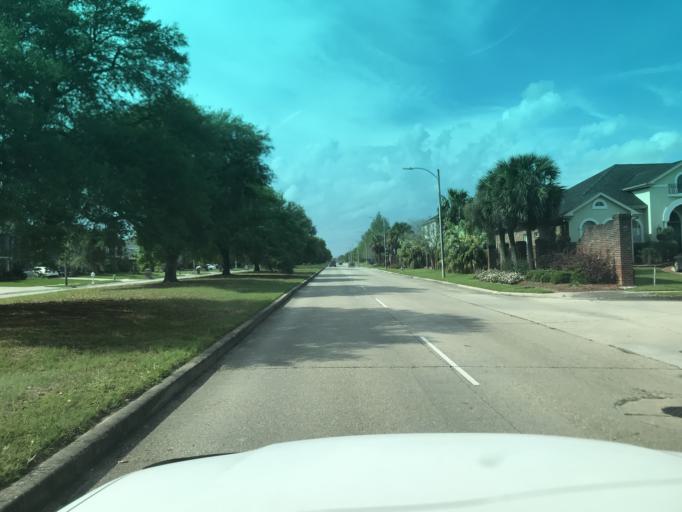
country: US
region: Louisiana
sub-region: Saint Bernard Parish
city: Chalmette
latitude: 30.0358
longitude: -89.9524
